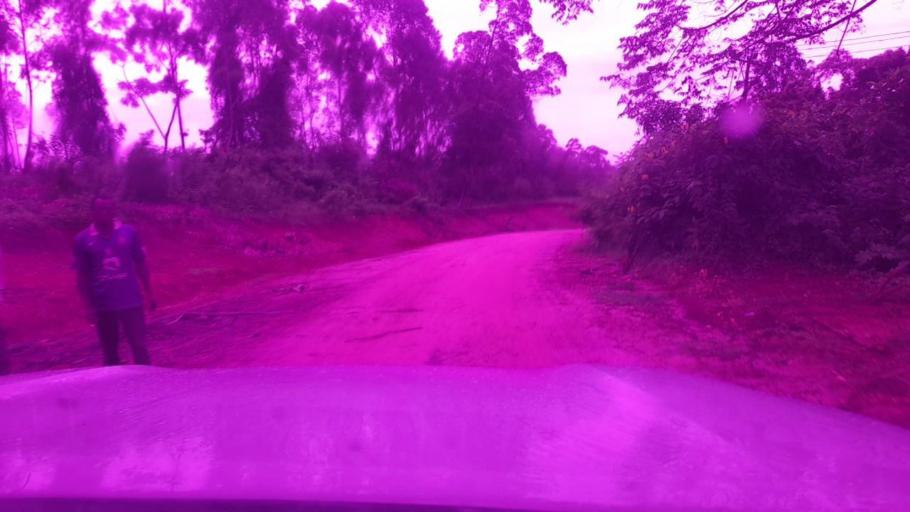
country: ET
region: Southern Nations, Nationalities, and People's Region
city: Bonga
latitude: 7.4451
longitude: 36.1456
